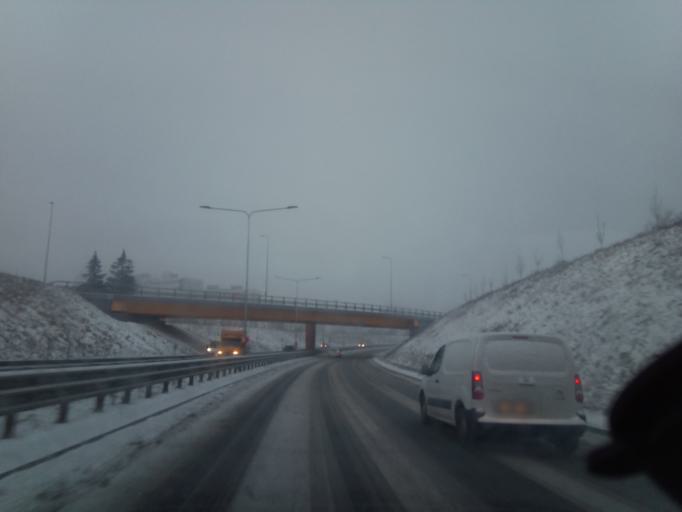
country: LT
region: Vilnius County
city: Pasilaiciai
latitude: 54.7452
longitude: 25.2184
